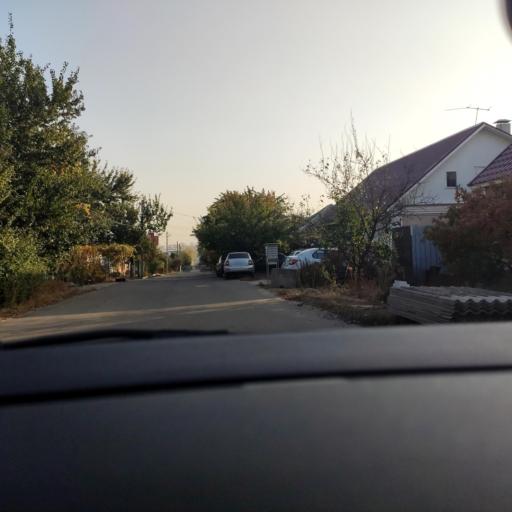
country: RU
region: Voronezj
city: Podgornoye
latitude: 51.6985
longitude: 39.1532
